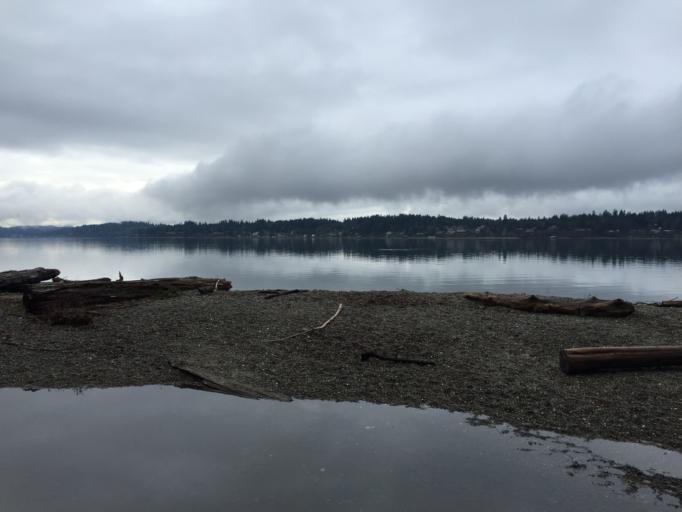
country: US
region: Washington
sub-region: Thurston County
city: Olympia
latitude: 47.1313
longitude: -122.9045
